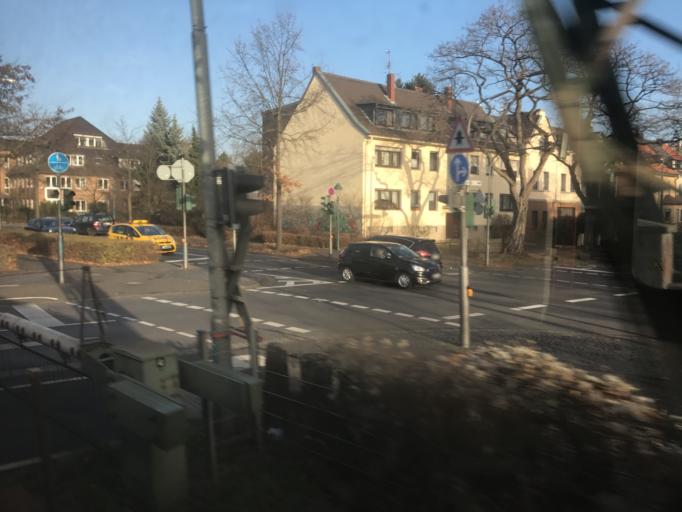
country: DE
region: North Rhine-Westphalia
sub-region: Regierungsbezirk Koln
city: Bonn
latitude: 50.7001
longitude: 7.1345
